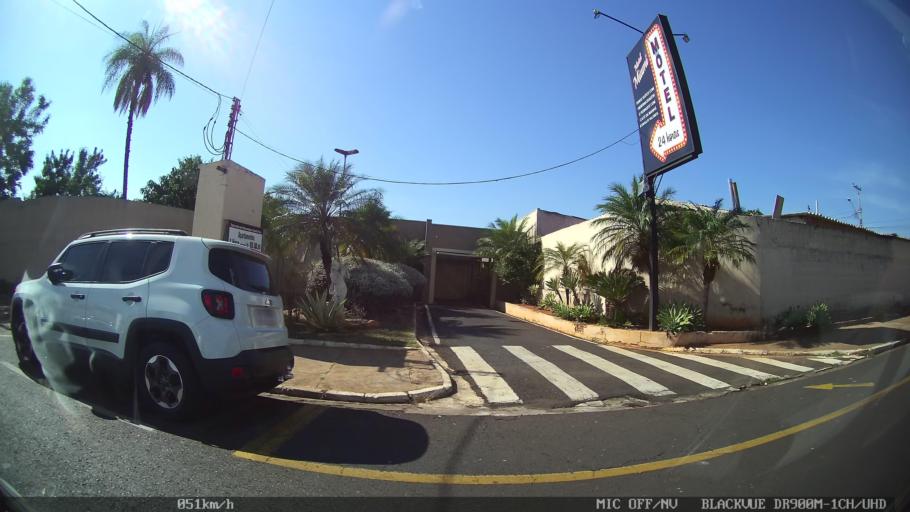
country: BR
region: Sao Paulo
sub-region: Sao Jose Do Rio Preto
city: Sao Jose do Rio Preto
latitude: -20.7802
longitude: -49.3863
